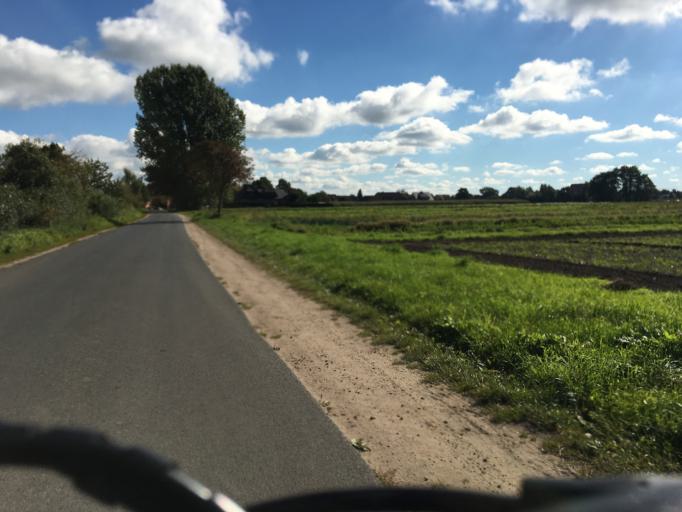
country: DE
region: Lower Saxony
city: Bardowick
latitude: 53.3083
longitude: 10.3820
